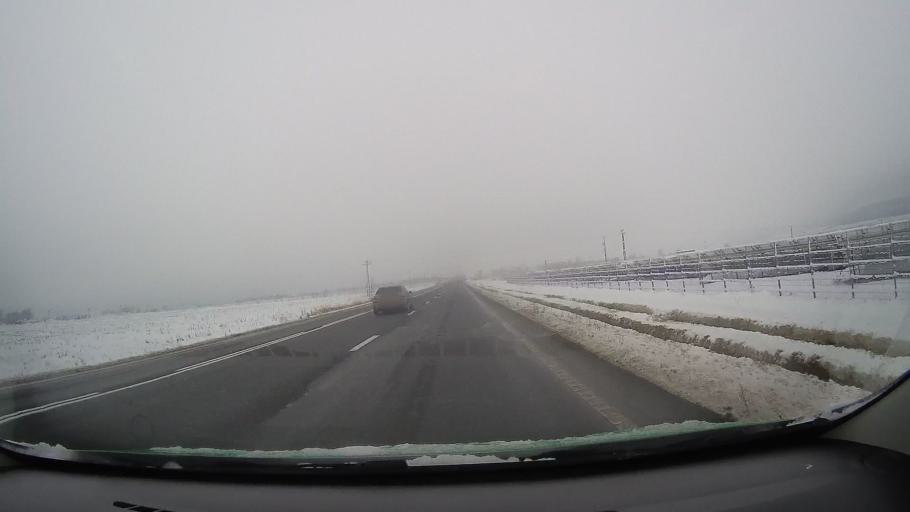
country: RO
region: Sibiu
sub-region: Oras Saliste
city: Saliste
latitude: 45.7905
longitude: 23.9232
